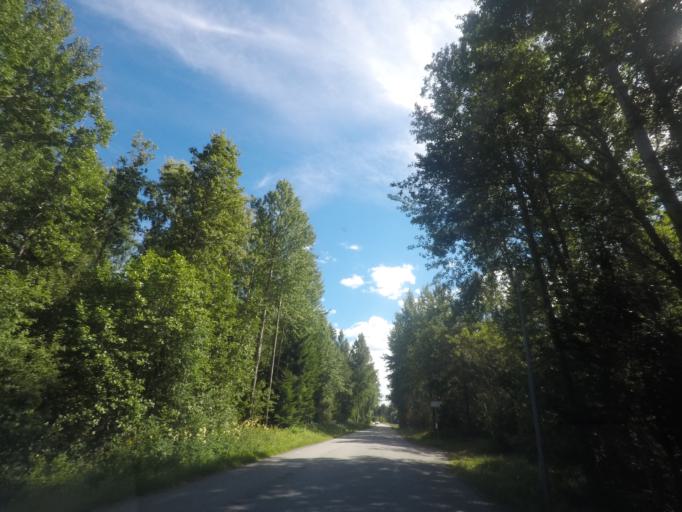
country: SE
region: Stockholm
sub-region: Norrtalje Kommun
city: Arno
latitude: 60.1638
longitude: 18.7628
